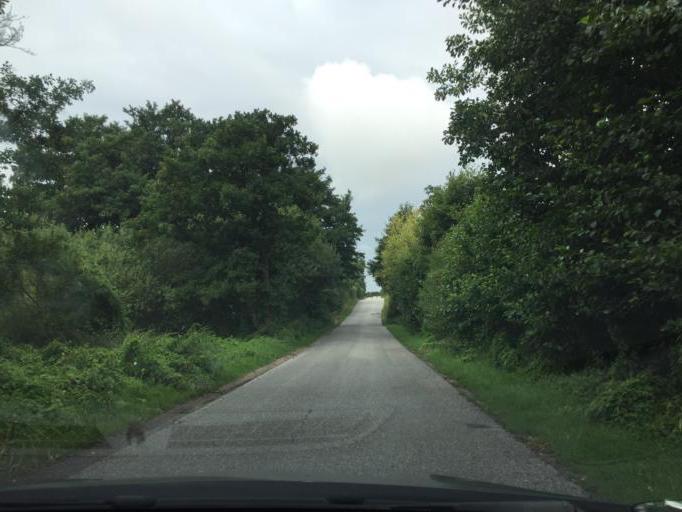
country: DK
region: South Denmark
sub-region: Assens Kommune
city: Harby
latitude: 55.2035
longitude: 10.0943
